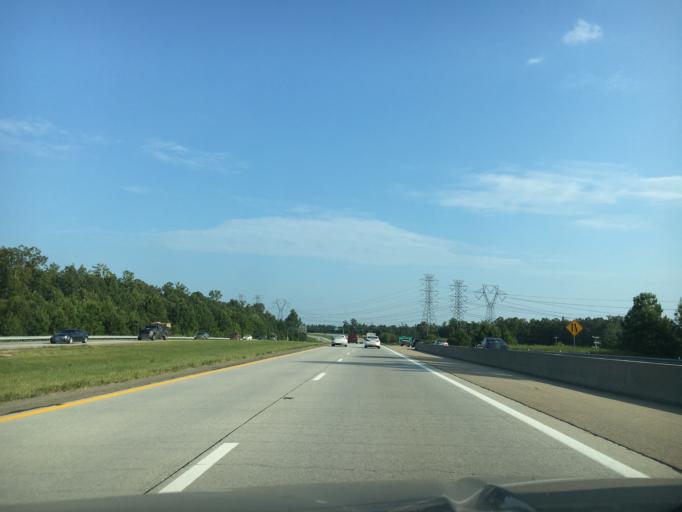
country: US
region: Virginia
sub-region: Chesterfield County
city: Brandermill
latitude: 37.4980
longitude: -77.6854
